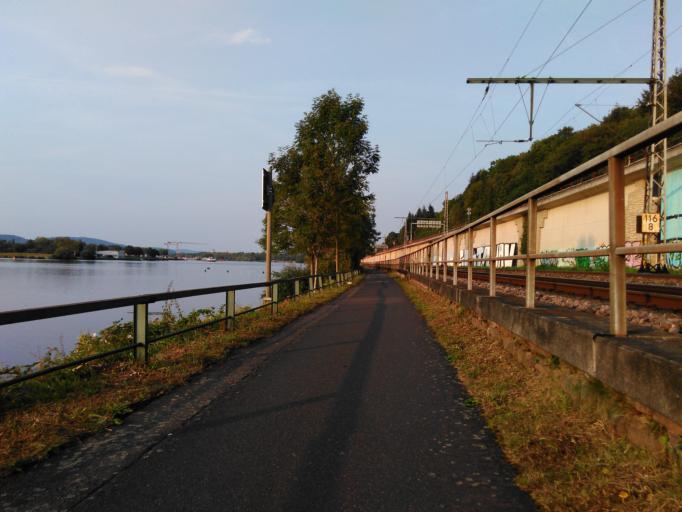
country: DE
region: Rheinland-Pfalz
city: Konz
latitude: 49.7186
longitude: 6.6126
